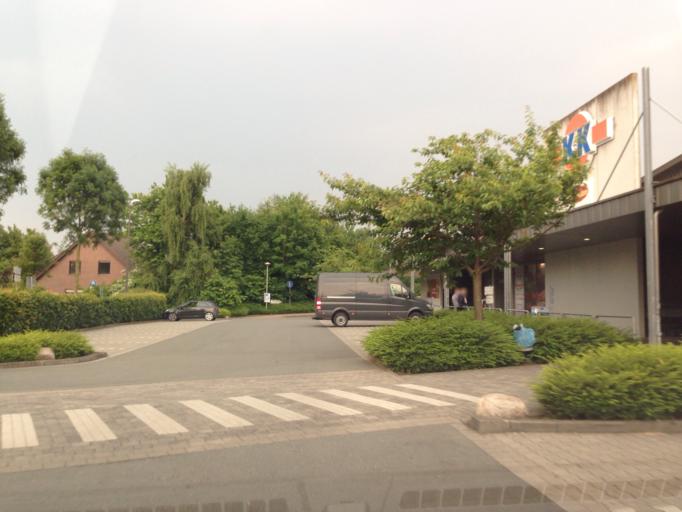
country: DE
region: North Rhine-Westphalia
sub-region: Regierungsbezirk Munster
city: Havixbeck
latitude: 51.9747
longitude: 7.4113
